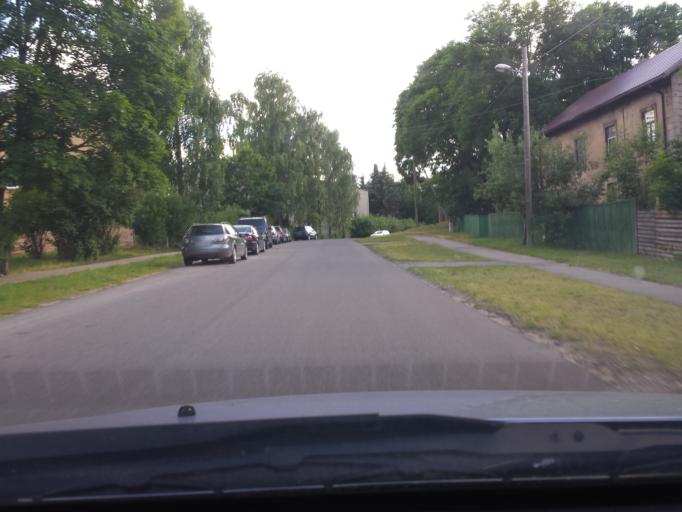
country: LV
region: Riga
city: Riga
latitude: 56.9598
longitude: 24.0635
